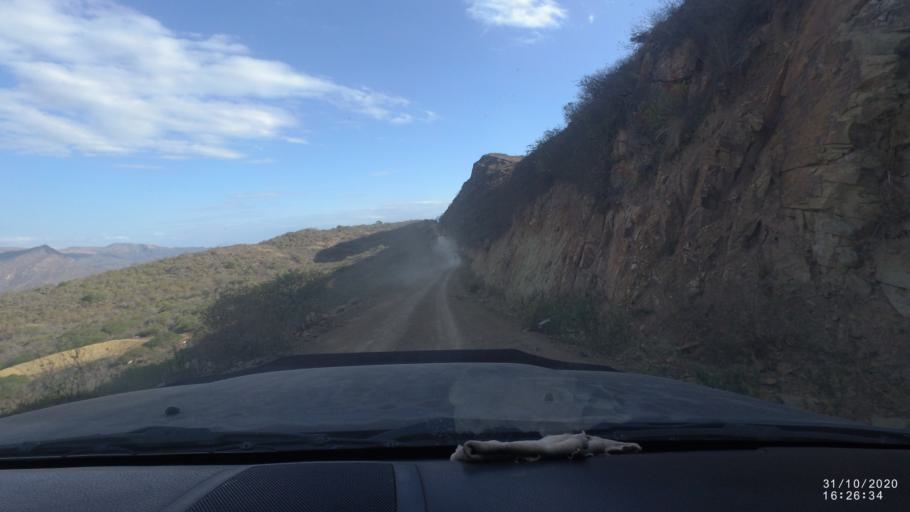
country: BO
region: Chuquisaca
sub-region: Provincia Zudanez
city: Mojocoya
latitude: -18.3991
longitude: -64.5863
